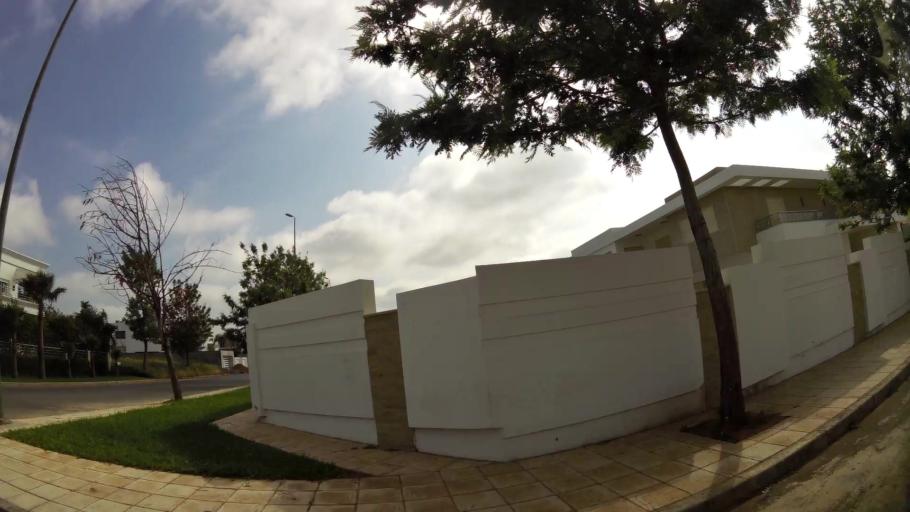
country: MA
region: Rabat-Sale-Zemmour-Zaer
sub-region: Rabat
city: Rabat
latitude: 33.9714
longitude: -6.8481
